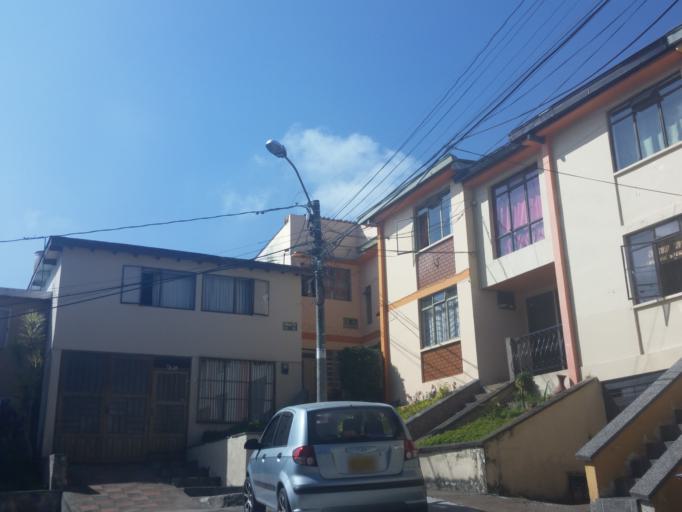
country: CO
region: Caldas
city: Manizales
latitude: 5.0781
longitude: -75.5267
